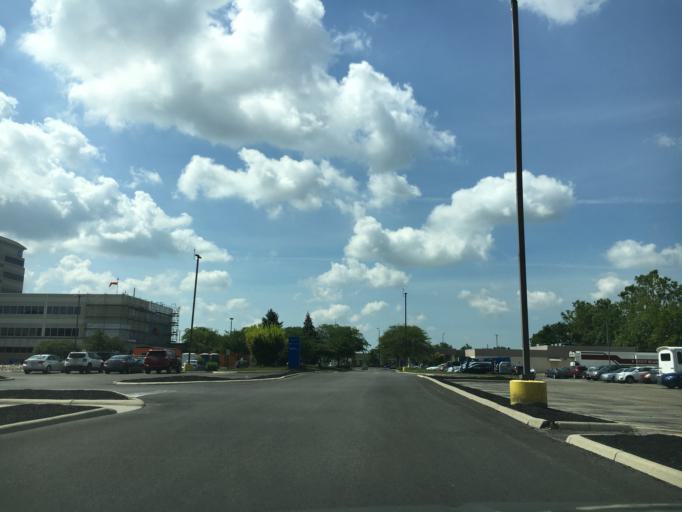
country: US
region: Ohio
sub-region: Franklin County
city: Lincoln Village
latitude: 39.9537
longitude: -83.1389
